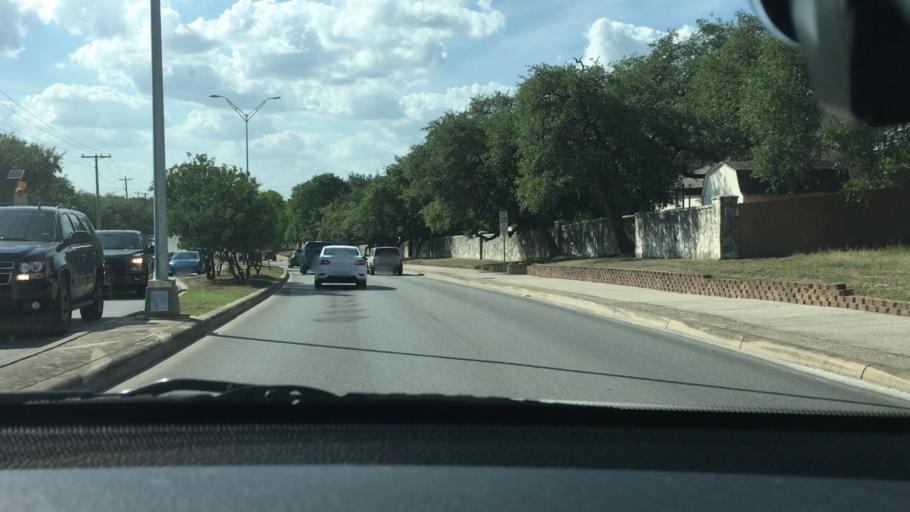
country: US
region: Texas
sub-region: Bexar County
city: Selma
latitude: 29.5821
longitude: -98.2826
